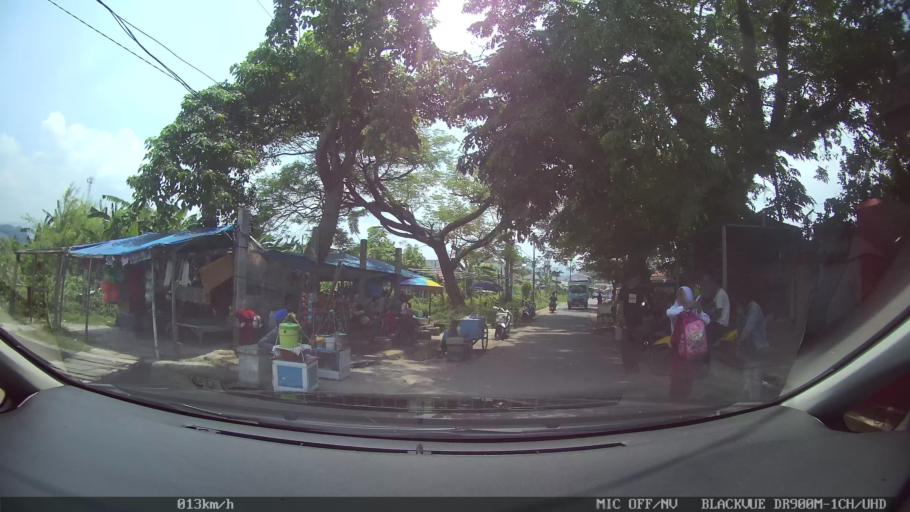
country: ID
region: Lampung
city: Bandarlampung
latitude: -5.4577
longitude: 105.2567
